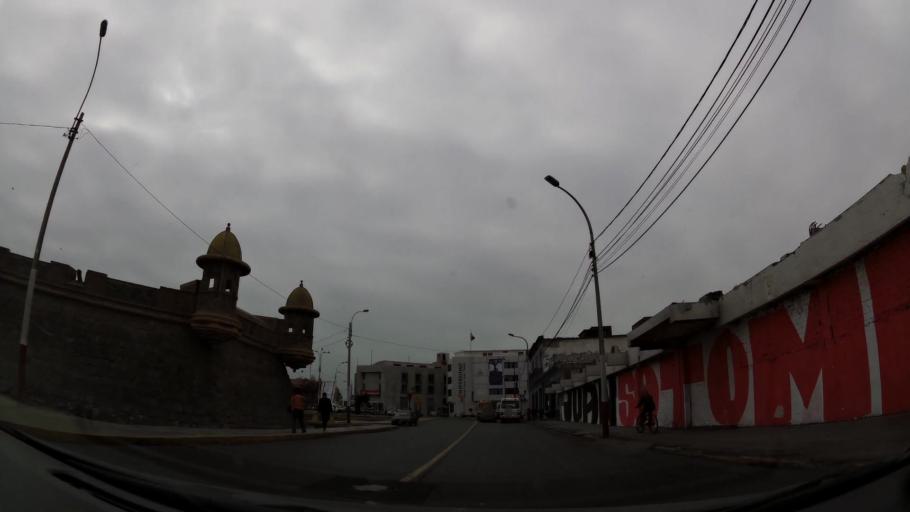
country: PE
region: Callao
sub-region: Callao
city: Callao
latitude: -12.0624
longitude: -77.1469
